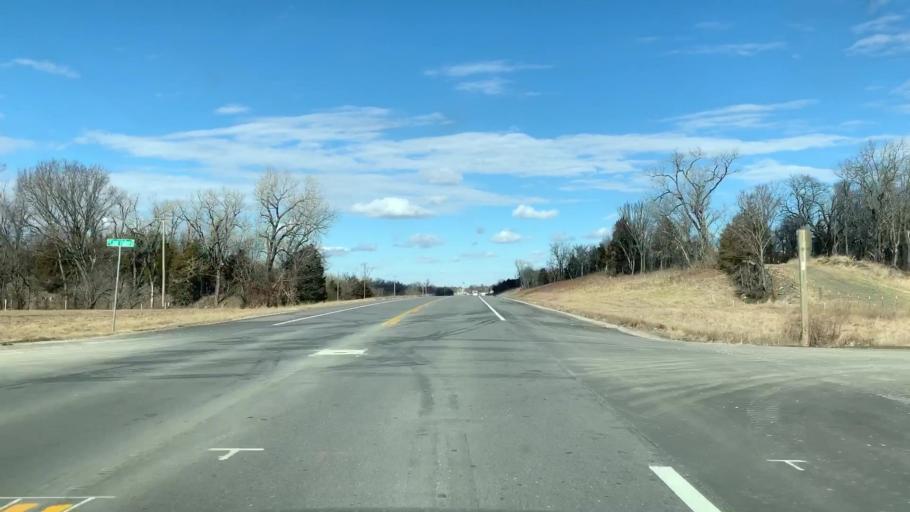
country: US
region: Kansas
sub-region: Crawford County
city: Pittsburg
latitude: 37.3250
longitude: -94.8322
